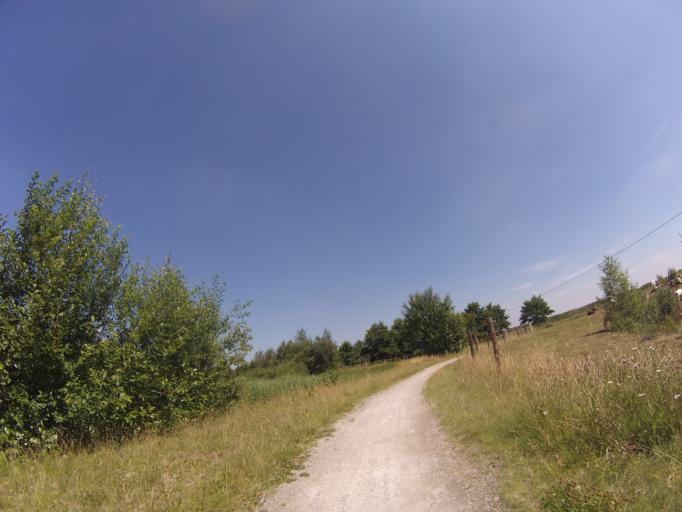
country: NL
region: Drenthe
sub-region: Gemeente Emmen
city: Klazienaveen
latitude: 52.7399
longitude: 7.0235
